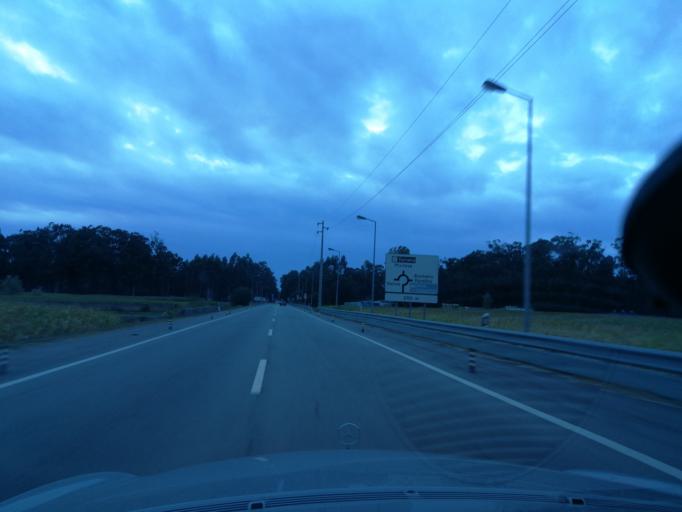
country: PT
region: Aveiro
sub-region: Murtosa
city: Murtosa
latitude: 40.7618
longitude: -8.6202
